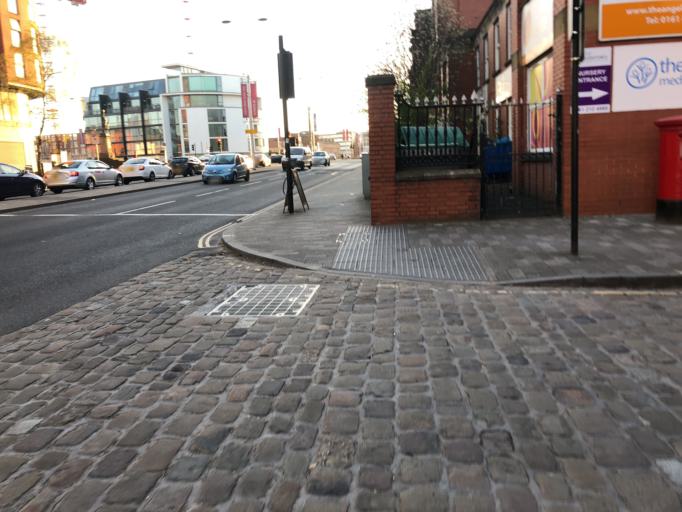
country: GB
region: England
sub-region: Manchester
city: Hulme
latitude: 53.4834
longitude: -2.2629
